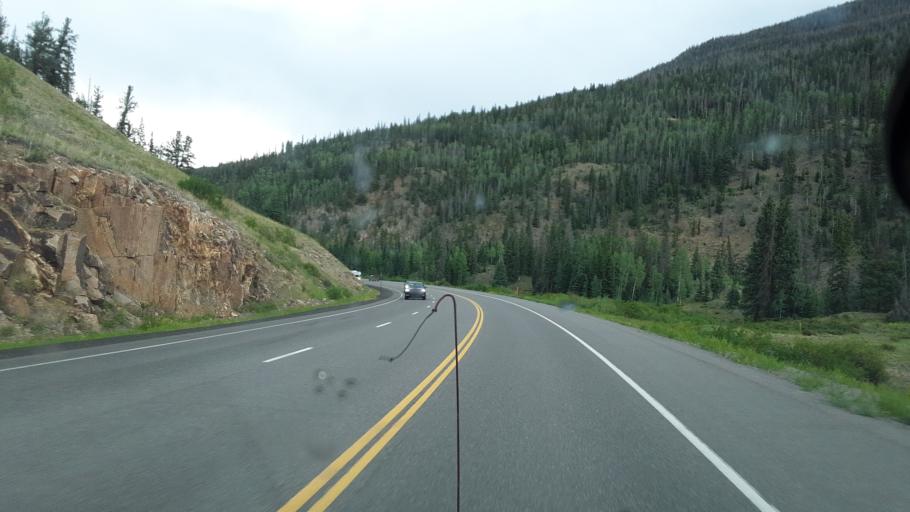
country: US
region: Colorado
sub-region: Archuleta County
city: Pagosa Springs
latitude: 37.5222
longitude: -106.7703
